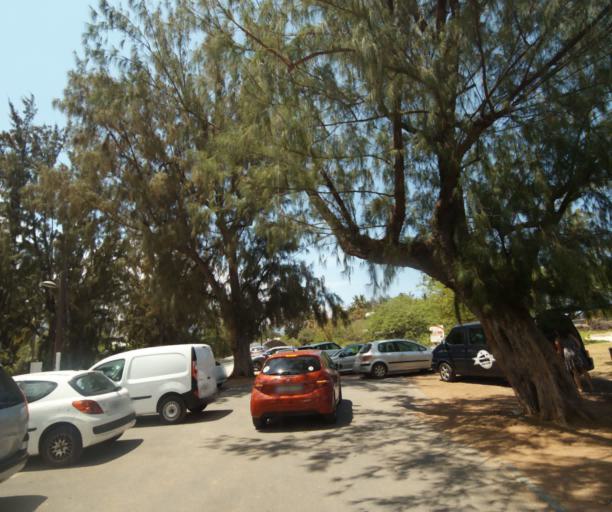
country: RE
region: Reunion
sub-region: Reunion
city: Trois-Bassins
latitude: -21.0835
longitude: 55.2266
